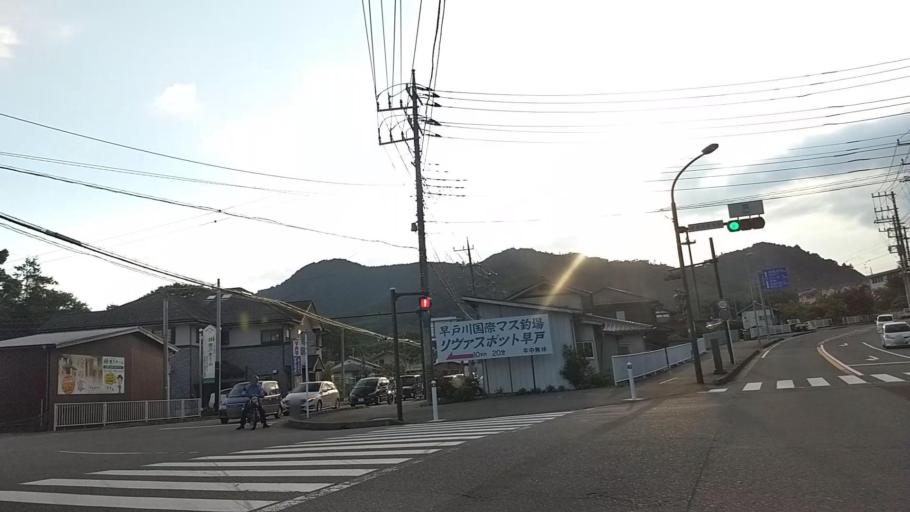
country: JP
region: Tokyo
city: Hachioji
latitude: 35.5662
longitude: 139.2456
